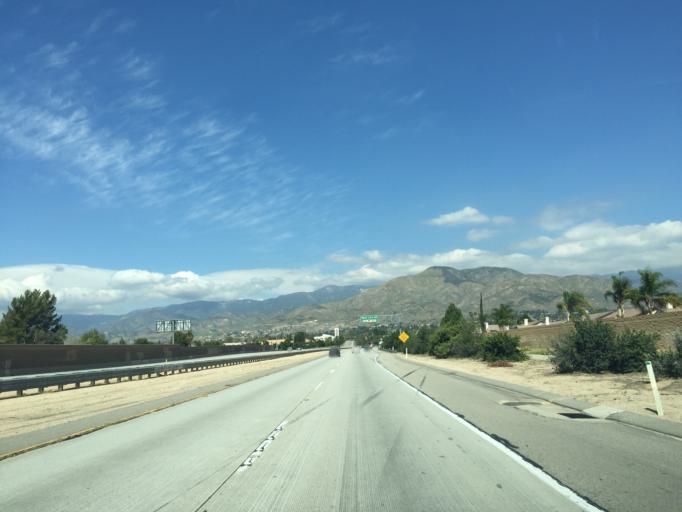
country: US
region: California
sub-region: San Bernardino County
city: Highland
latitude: 34.1138
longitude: -117.1997
